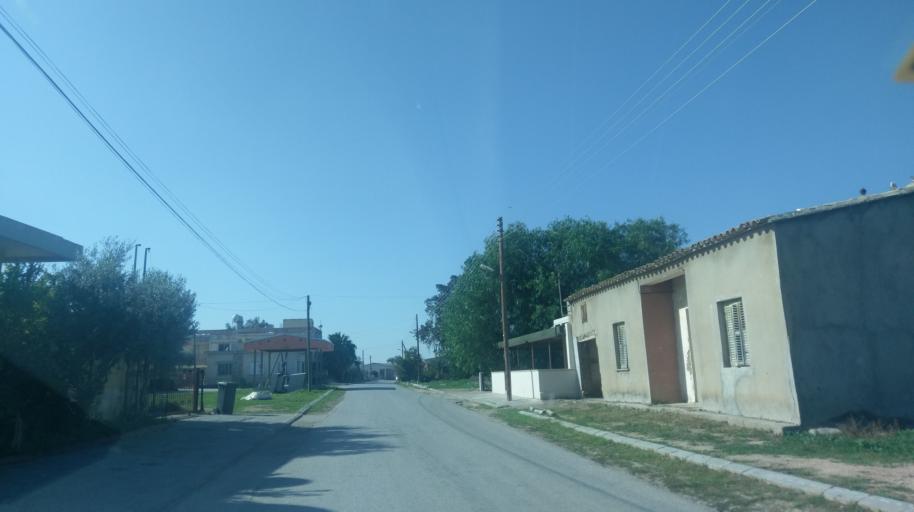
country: CY
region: Ammochostos
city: Lefkonoiko
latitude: 35.2612
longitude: 33.7838
